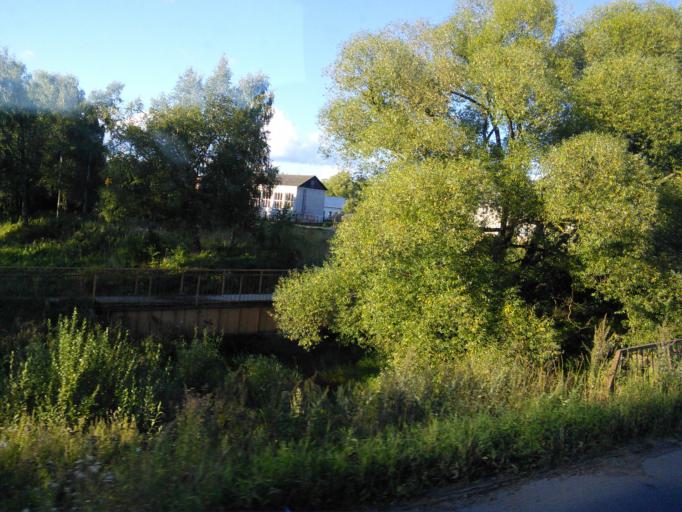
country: RU
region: Jaroslavl
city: Poshekhon'ye
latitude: 58.4975
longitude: 39.1202
